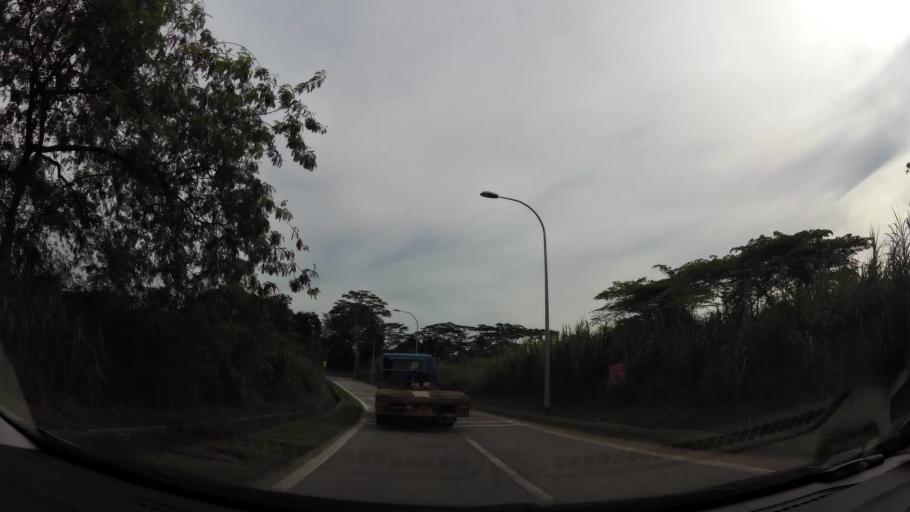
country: MY
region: Johor
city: Johor Bahru
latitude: 1.4177
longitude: 103.7161
